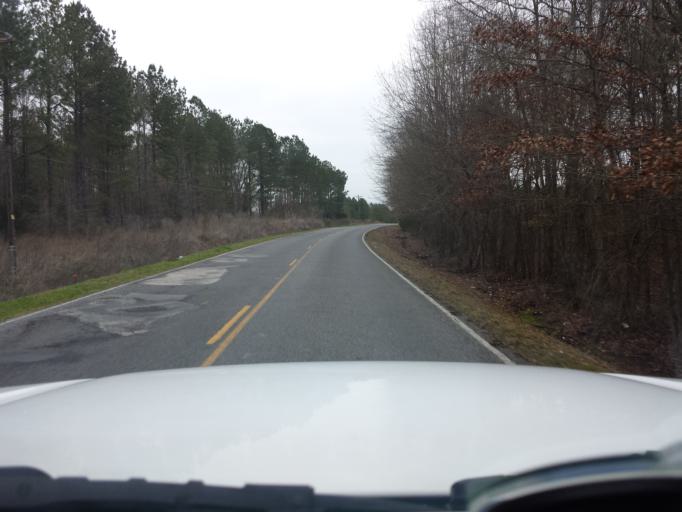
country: US
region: Mississippi
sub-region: Yazoo County
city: Yazoo City
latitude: 32.7947
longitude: -90.2047
